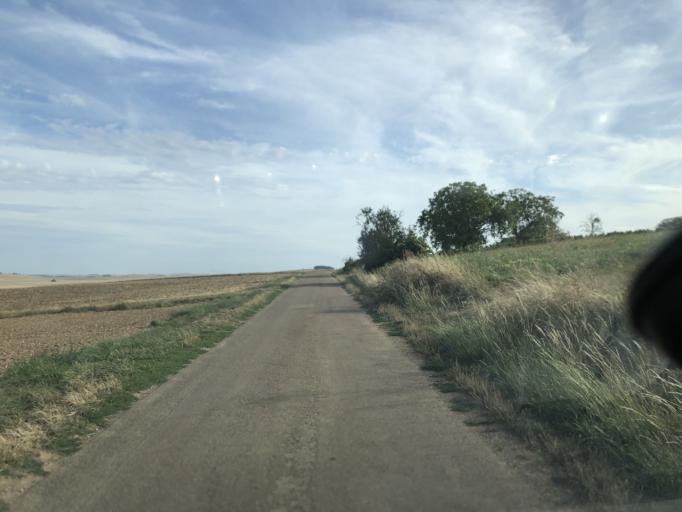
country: FR
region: Bourgogne
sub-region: Departement de l'Yonne
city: Joigny
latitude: 47.9358
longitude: 3.3872
